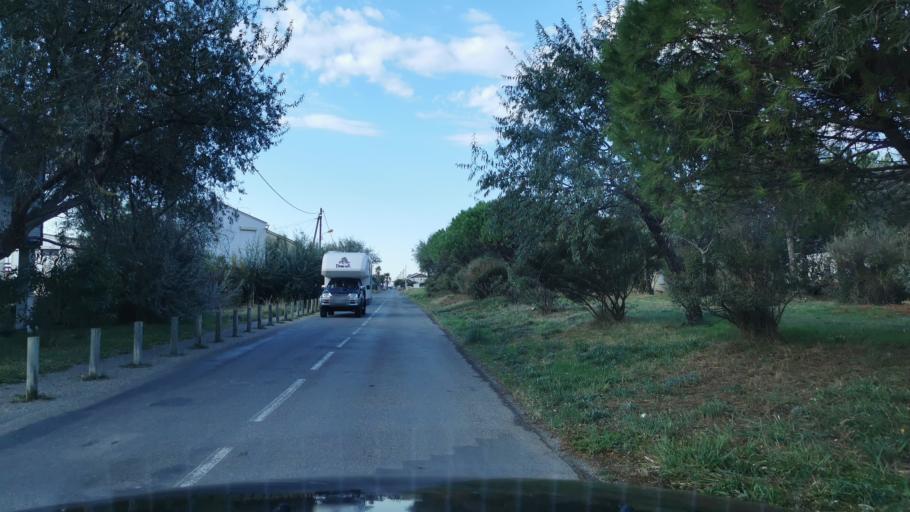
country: FR
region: Languedoc-Roussillon
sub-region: Departement de l'Aude
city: Gruissan
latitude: 43.1029
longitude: 3.1119
